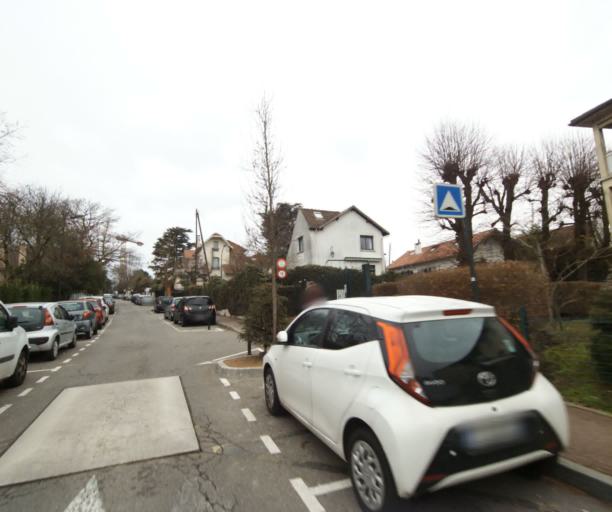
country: FR
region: Ile-de-France
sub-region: Departement des Hauts-de-Seine
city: Garches
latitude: 48.8465
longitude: 2.1838
